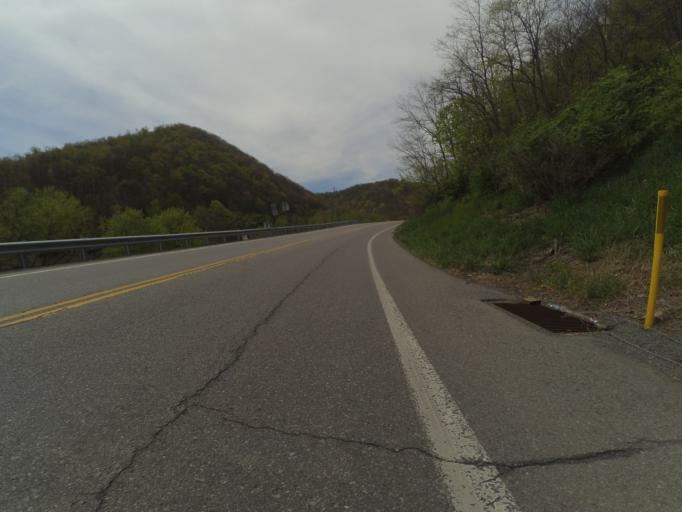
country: US
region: Pennsylvania
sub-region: Blair County
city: Tyrone
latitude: 40.6654
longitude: -78.2229
